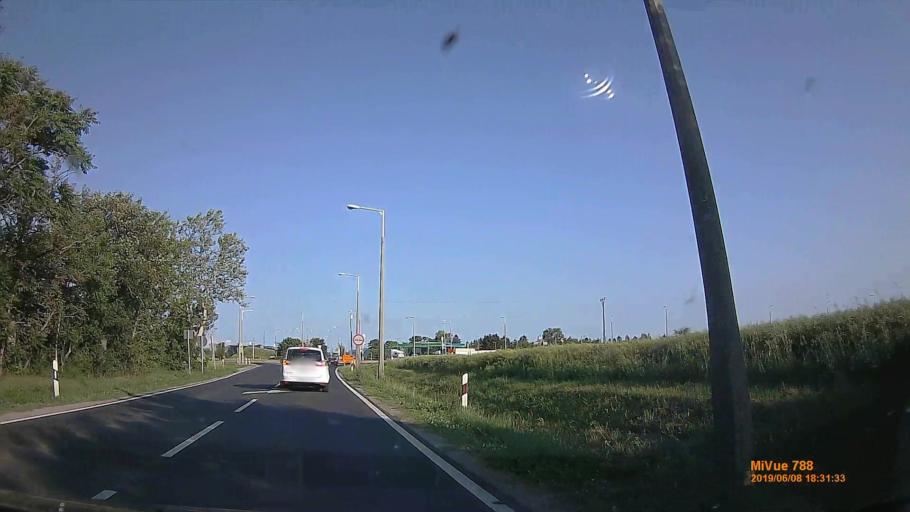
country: HU
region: Vas
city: Sarvar
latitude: 47.3616
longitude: 16.8965
